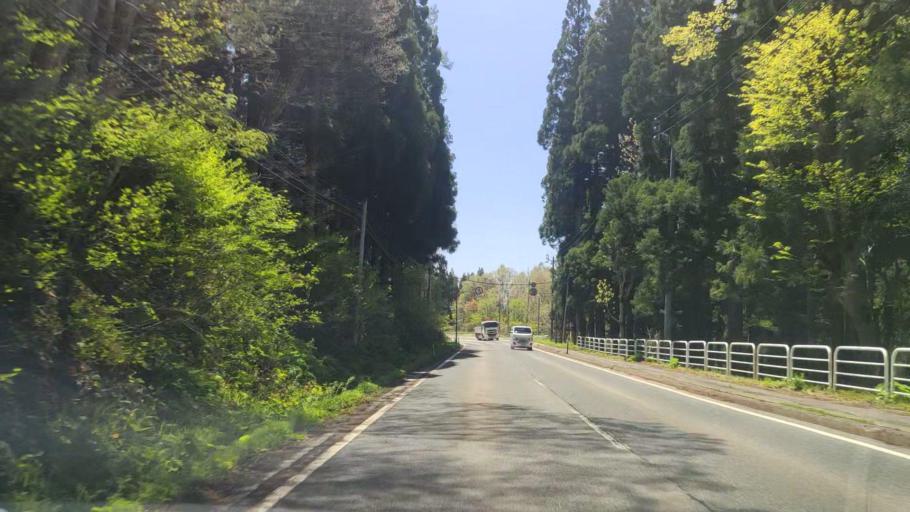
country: JP
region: Yamagata
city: Shinjo
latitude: 38.8933
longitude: 140.3242
